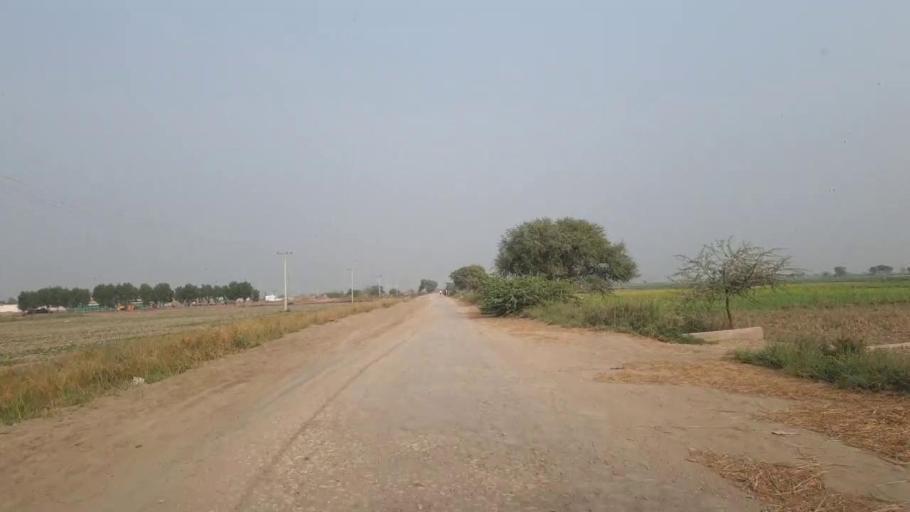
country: PK
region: Sindh
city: Mirpur Batoro
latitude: 24.5674
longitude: 68.4126
